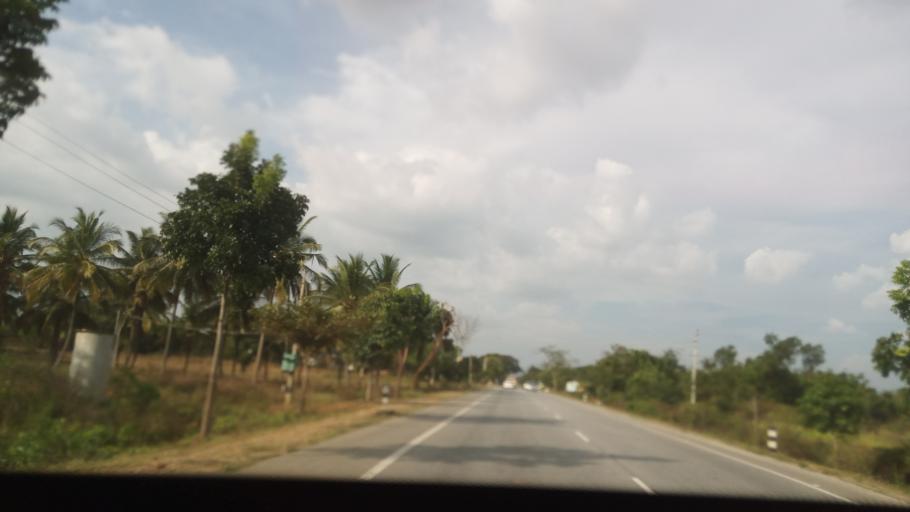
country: IN
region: Karnataka
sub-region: Tumkur
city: Kunigal
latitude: 12.8625
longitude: 77.0396
